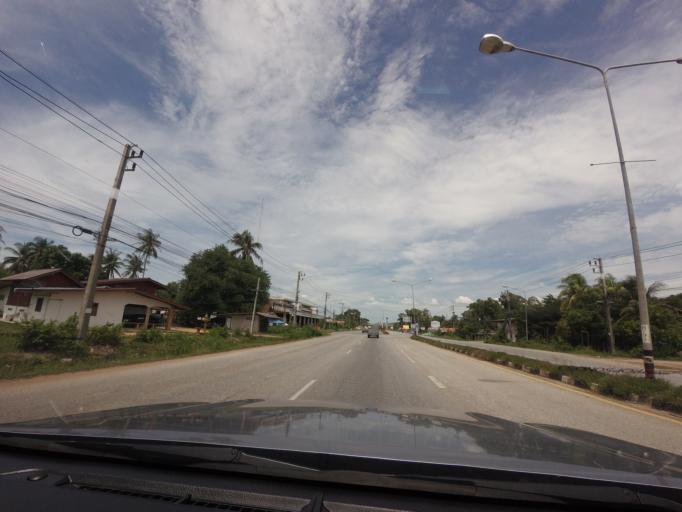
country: TH
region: Songkhla
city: Singhanakhon
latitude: 7.2424
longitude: 100.5449
